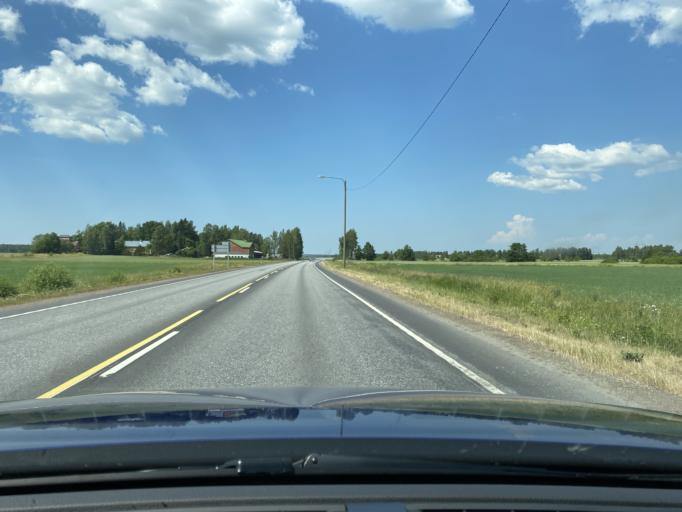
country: FI
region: Satakunta
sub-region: Rauma
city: Eura
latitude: 61.1466
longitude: 22.1040
